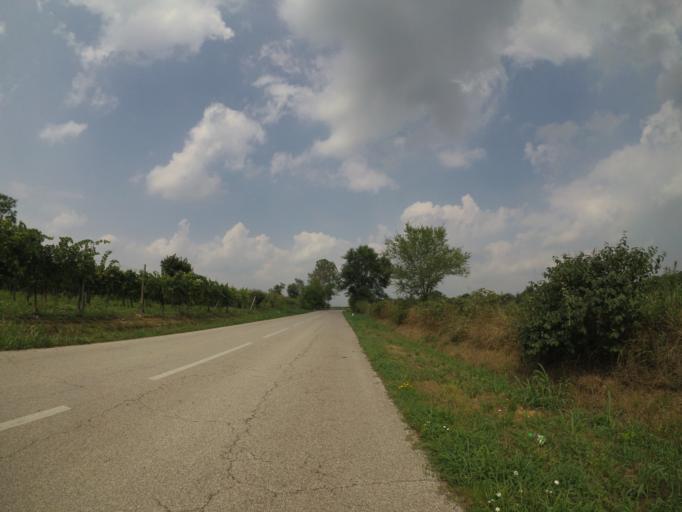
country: IT
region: Friuli Venezia Giulia
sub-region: Provincia di Udine
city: Sedegliano
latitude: 46.0080
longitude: 13.0047
